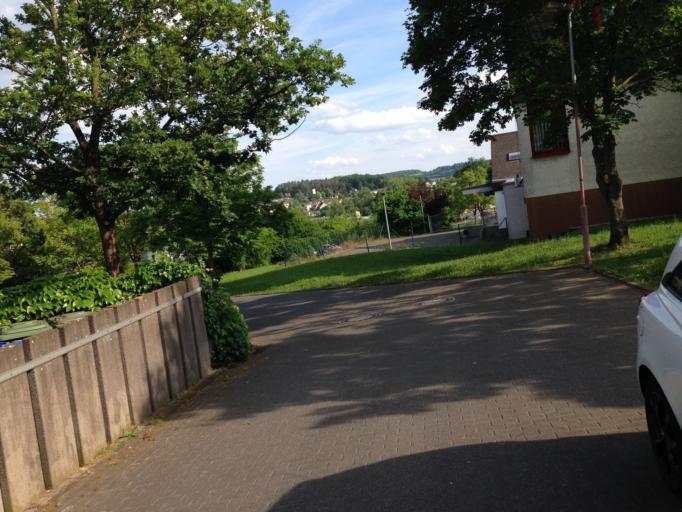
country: DE
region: Hesse
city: Staufenberg
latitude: 50.6593
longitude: 8.7341
